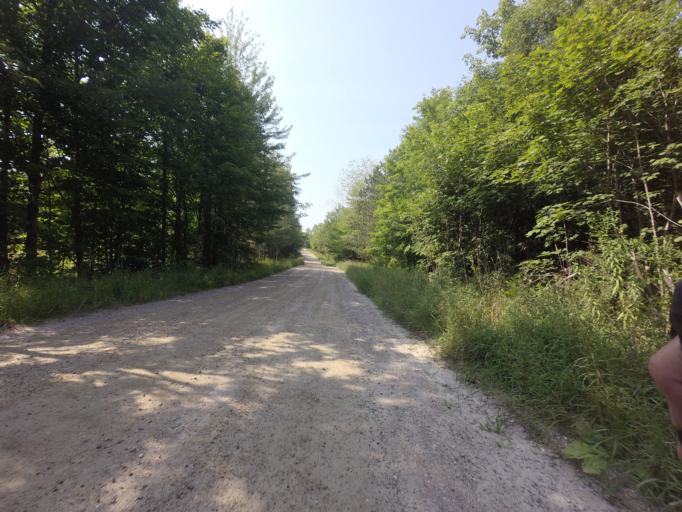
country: CA
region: Ontario
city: Skatepark
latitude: 44.7218
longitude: -76.7759
